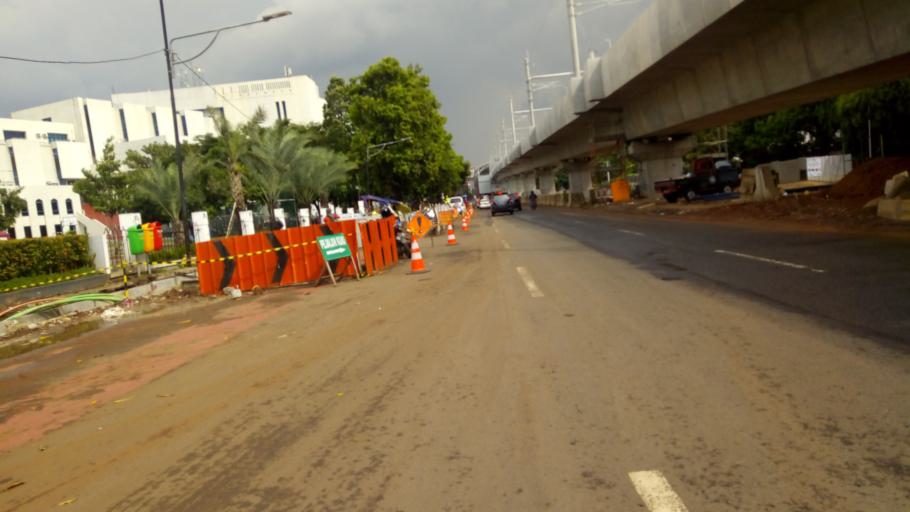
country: ID
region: Jakarta Raya
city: Jakarta
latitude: -6.2349
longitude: 106.7985
